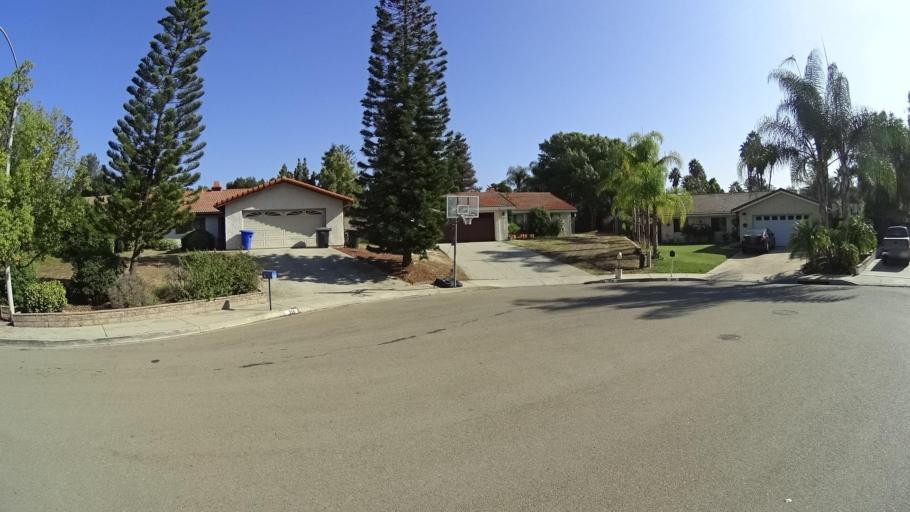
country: US
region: California
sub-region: San Diego County
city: Fallbrook
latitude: 33.3733
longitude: -117.2392
